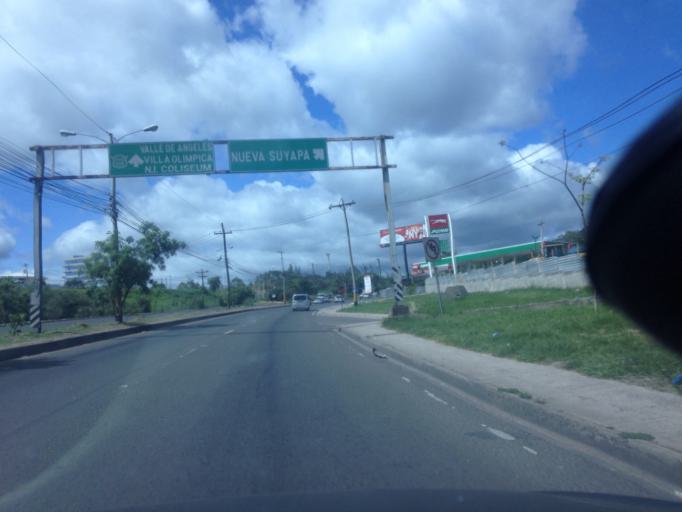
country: HN
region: Francisco Morazan
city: Tegucigalpa
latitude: 14.0799
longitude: -87.1646
